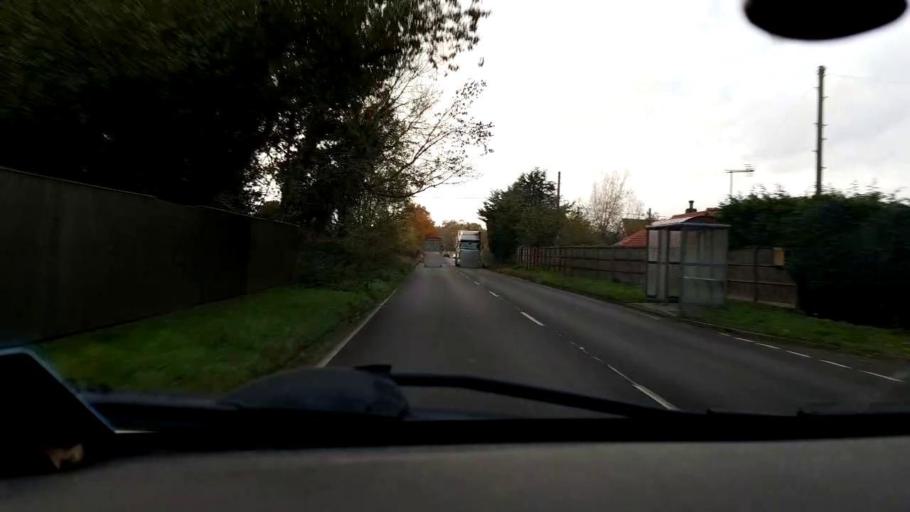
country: GB
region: England
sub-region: Norfolk
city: Costessey
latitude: 52.7067
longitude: 1.1480
